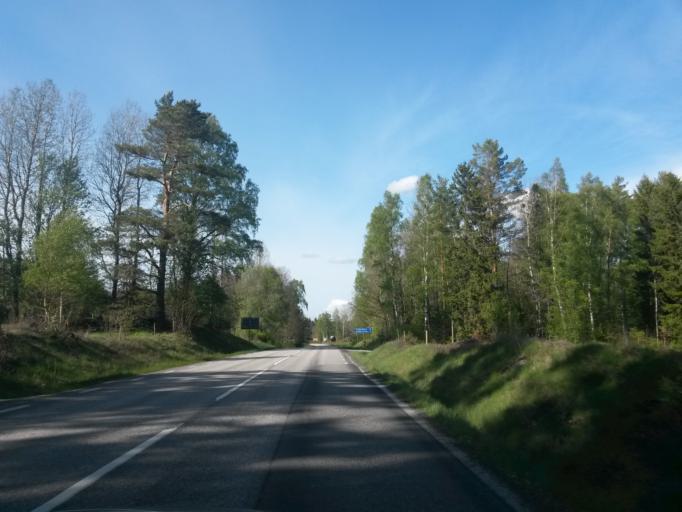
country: SE
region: Vaestra Goetaland
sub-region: Herrljunga Kommun
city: Herrljunga
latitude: 58.0590
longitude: 13.0421
